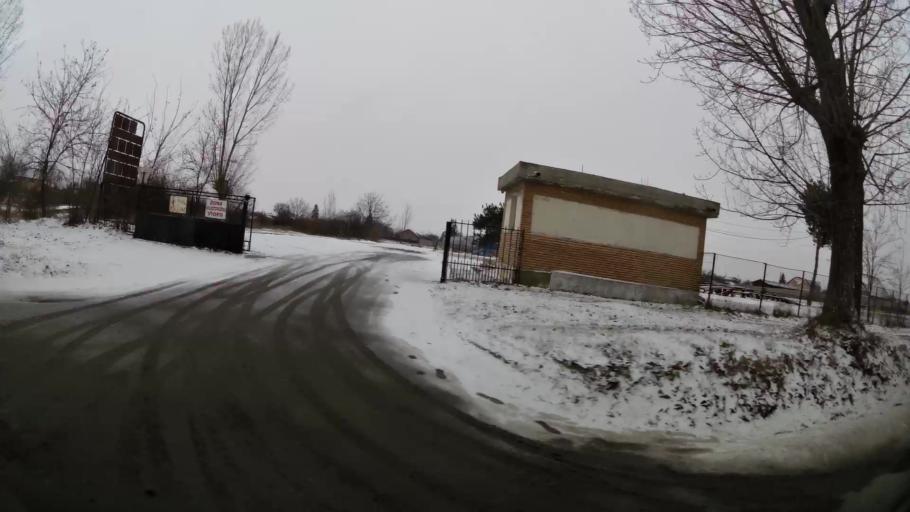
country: RO
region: Dambovita
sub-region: Comuna Ulmi
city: Ulmi
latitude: 44.9014
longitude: 25.5003
